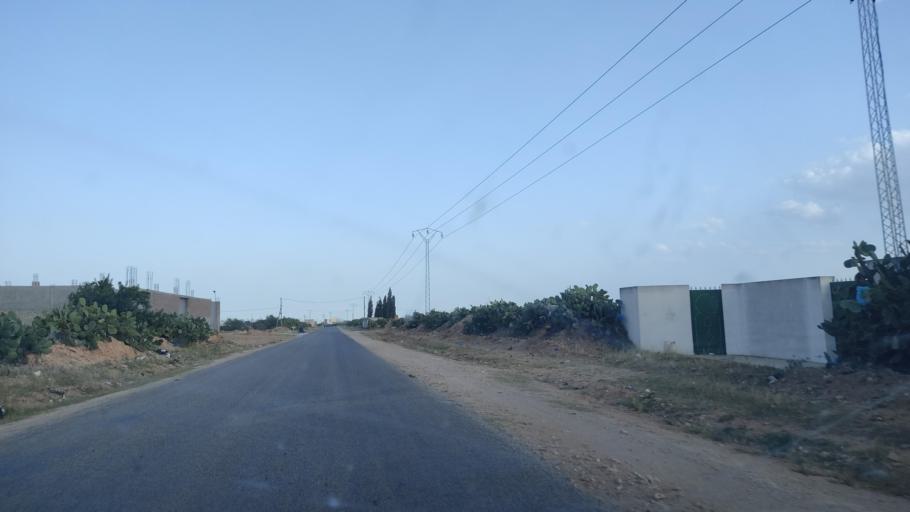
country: TN
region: Safaqis
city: Sfax
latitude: 34.8161
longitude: 10.6555
